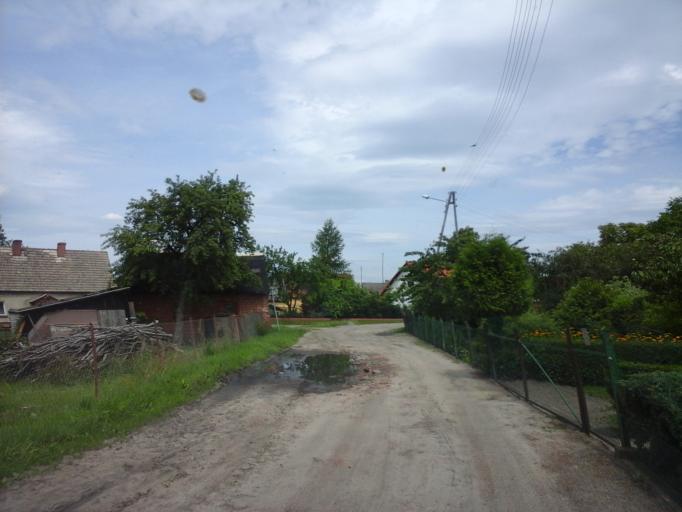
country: PL
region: Lubusz
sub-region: Powiat strzelecko-drezdenecki
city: Dobiegniew
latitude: 53.0772
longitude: 15.7844
